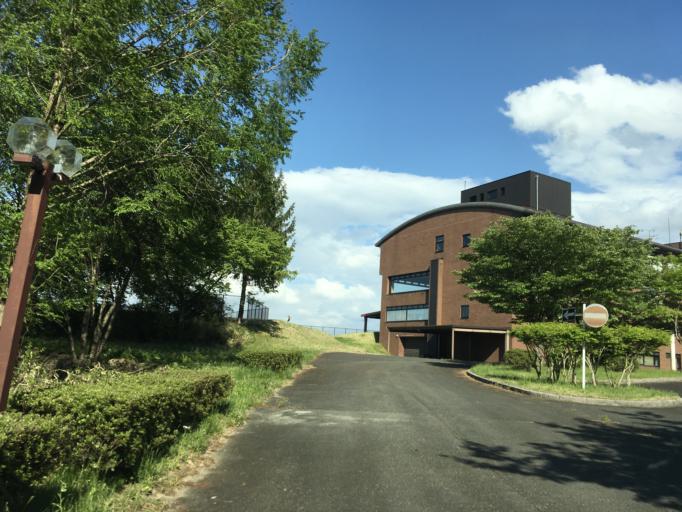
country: JP
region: Iwate
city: Mizusawa
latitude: 39.1646
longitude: 141.0682
